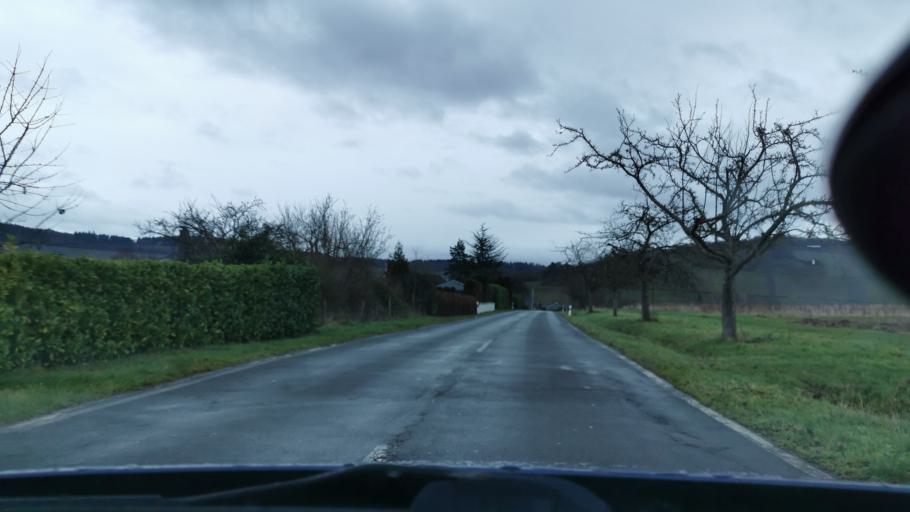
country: DE
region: Rheinland-Pfalz
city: Brauneberg
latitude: 49.9268
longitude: 6.9889
